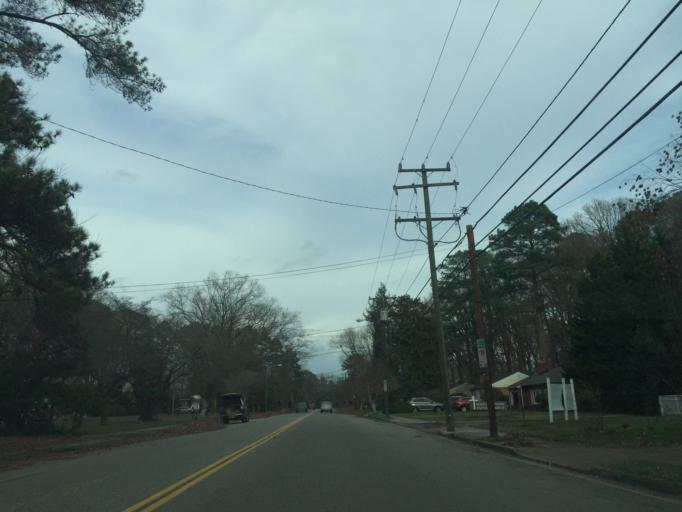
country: US
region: Virginia
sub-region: City of Newport News
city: Newport News
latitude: 37.0579
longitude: -76.4980
